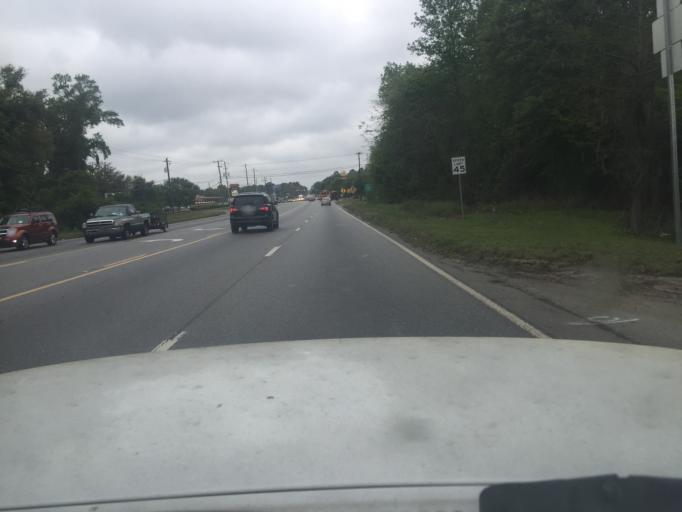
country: US
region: Georgia
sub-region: Chatham County
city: Garden City
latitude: 32.0493
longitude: -81.1620
